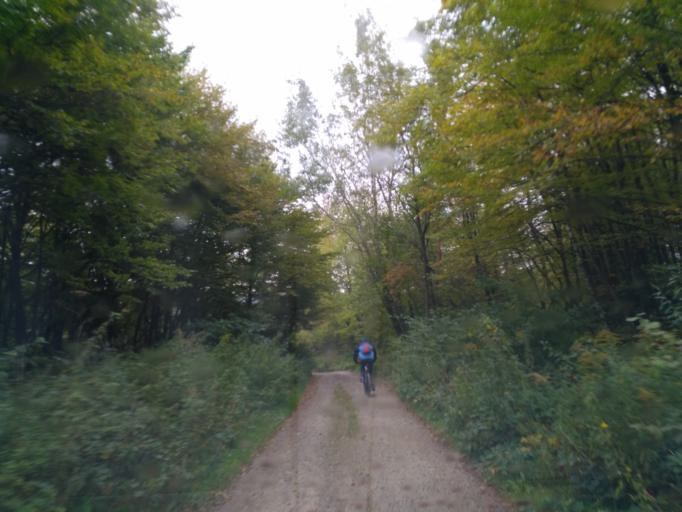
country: SK
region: Kosicky
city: Kosice
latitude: 48.7705
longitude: 21.2877
